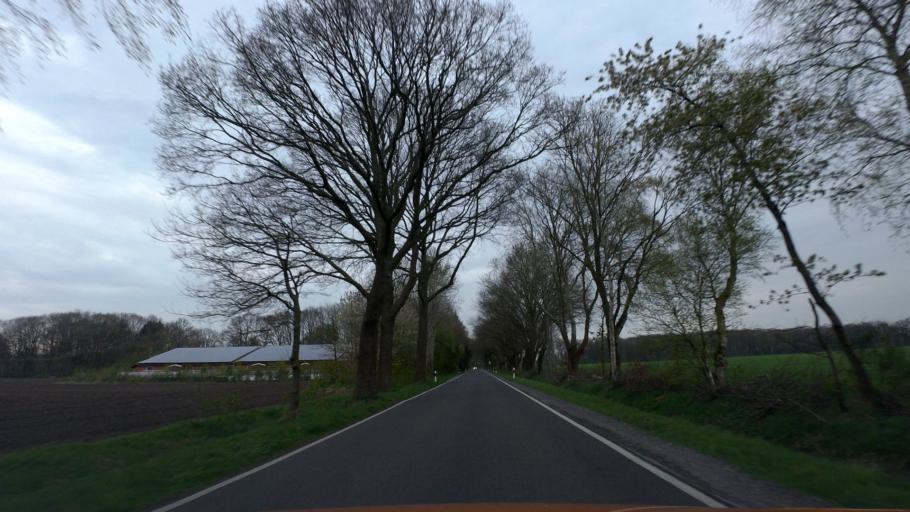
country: DE
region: Lower Saxony
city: Cloppenburg
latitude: 52.7730
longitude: 8.0207
